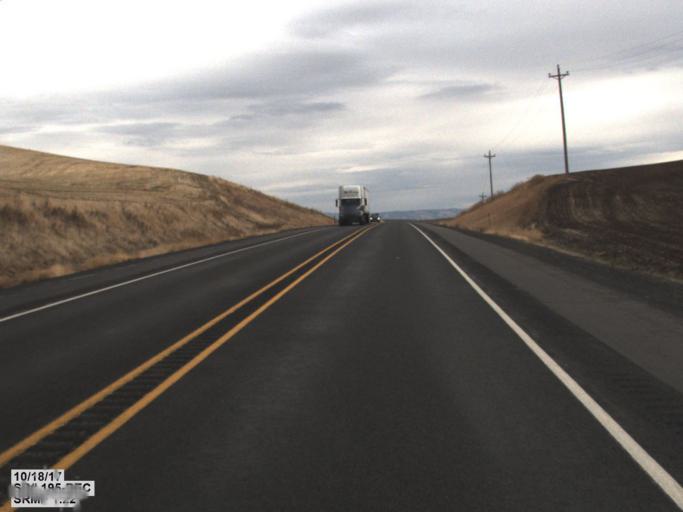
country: US
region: Washington
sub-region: Asotin County
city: Clarkston
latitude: 46.4845
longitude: -117.0664
